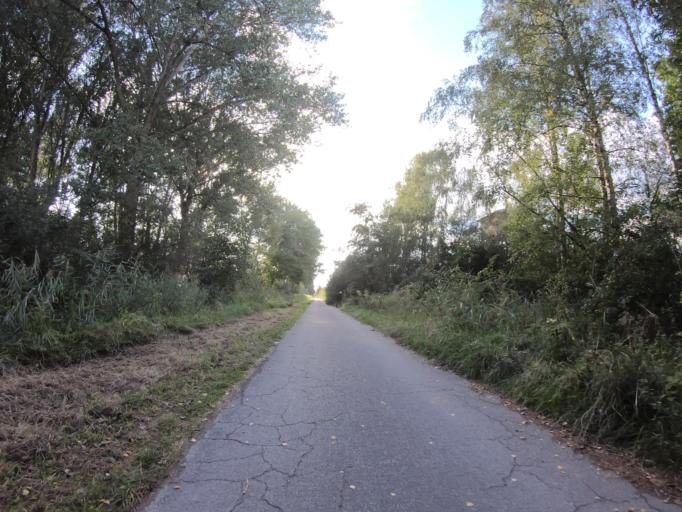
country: DE
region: Lower Saxony
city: Calberlah
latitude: 52.4256
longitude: 10.6667
